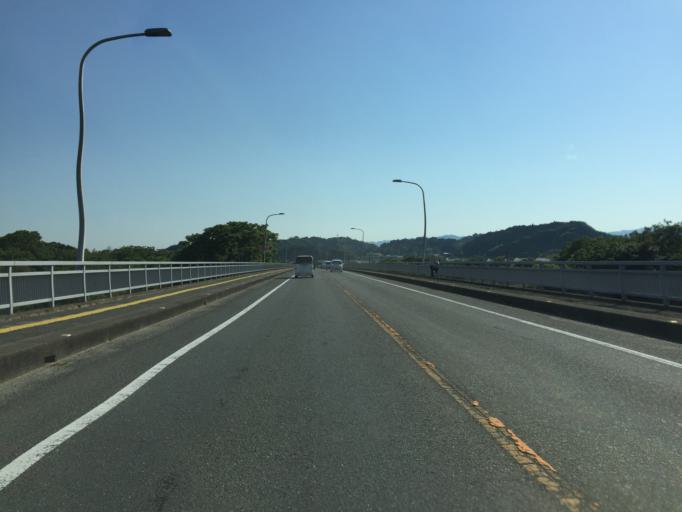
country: JP
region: Ibaraki
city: Kitaibaraki
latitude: 36.9186
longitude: 140.7782
